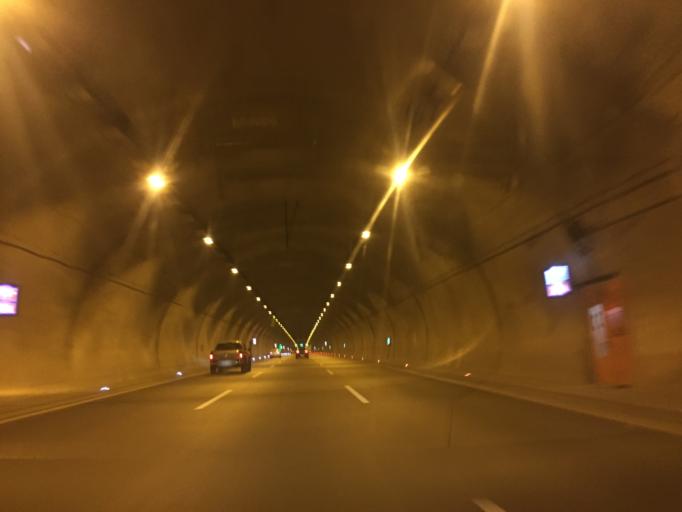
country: TR
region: Bursa
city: Demirtas
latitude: 40.3250
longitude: 29.0961
